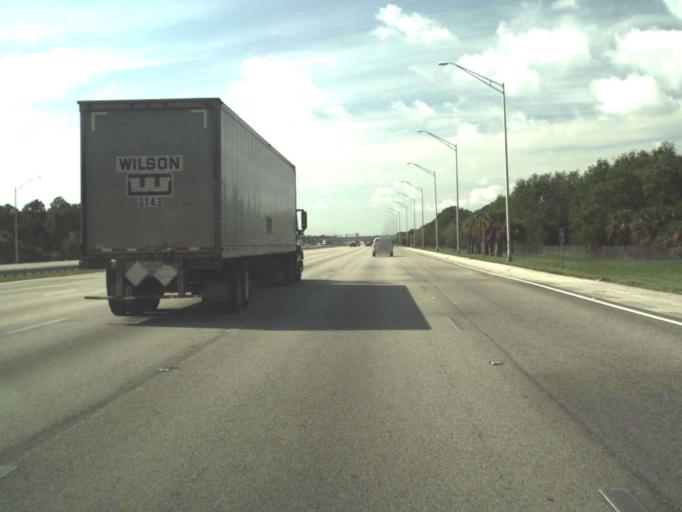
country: US
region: Florida
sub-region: Palm Beach County
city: Palm Beach Gardens
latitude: 26.8738
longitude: -80.1233
